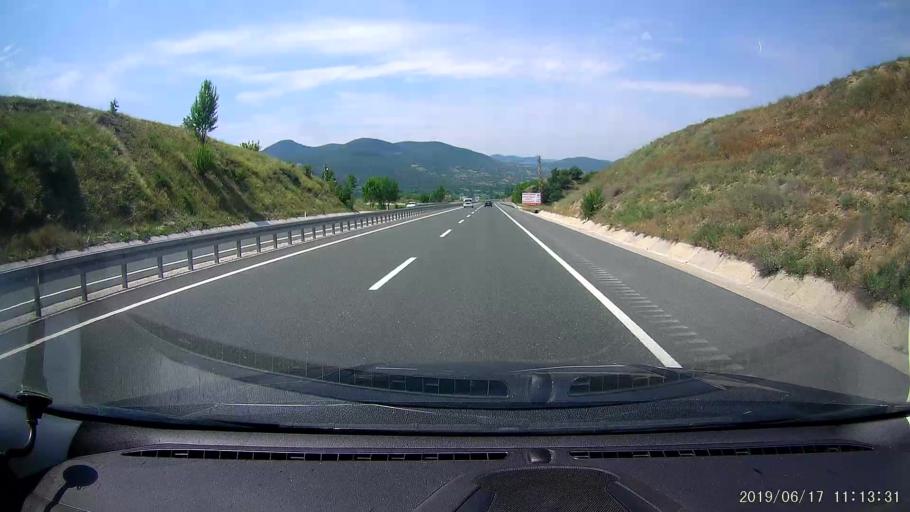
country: TR
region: Kastamonu
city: Tosya
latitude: 40.9610
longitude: 33.9707
